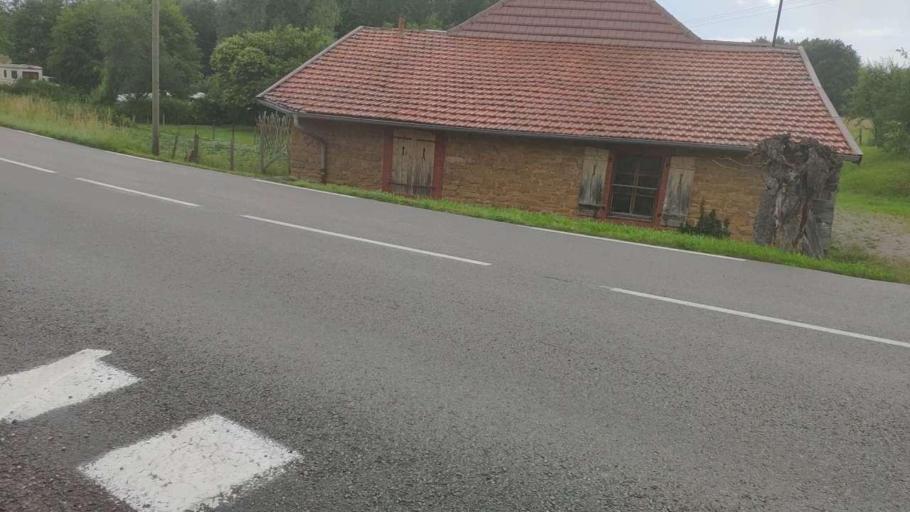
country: FR
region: Franche-Comte
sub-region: Departement du Jura
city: Mont-sous-Vaudrey
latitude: 46.8712
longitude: 5.5386
